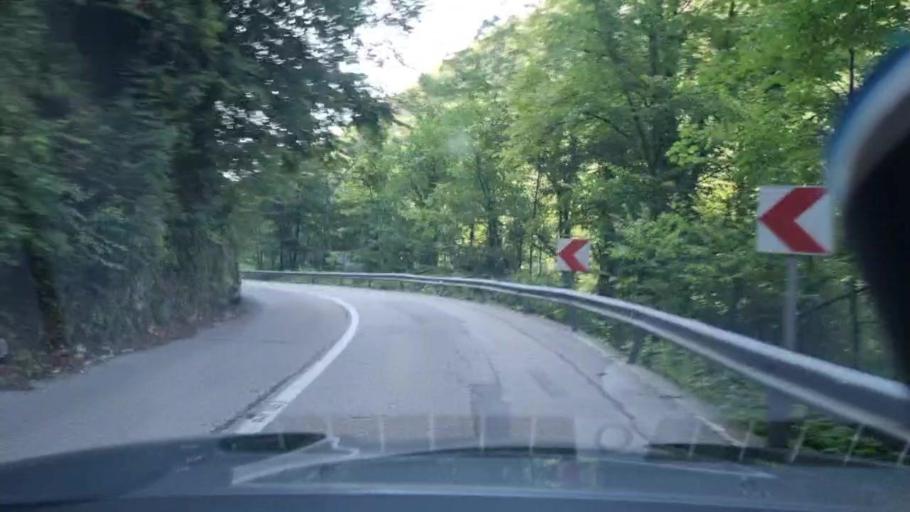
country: BA
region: Federation of Bosnia and Herzegovina
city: Bosanska Krupa
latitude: 44.8709
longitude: 16.0860
